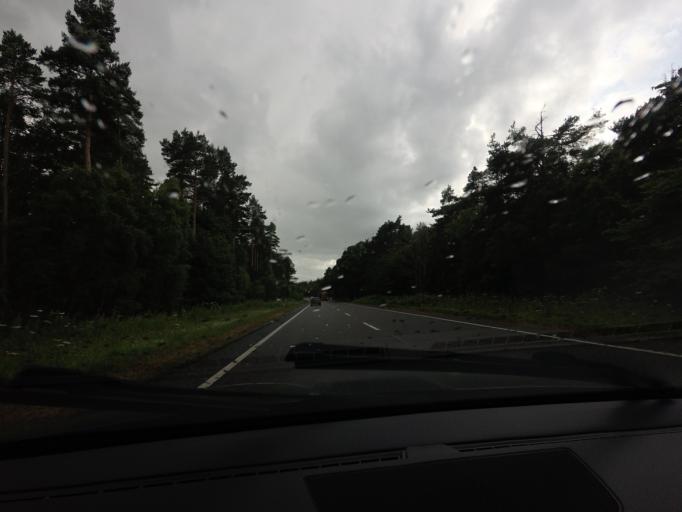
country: GB
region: Scotland
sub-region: Highland
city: Fortrose
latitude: 57.5281
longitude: -4.0550
